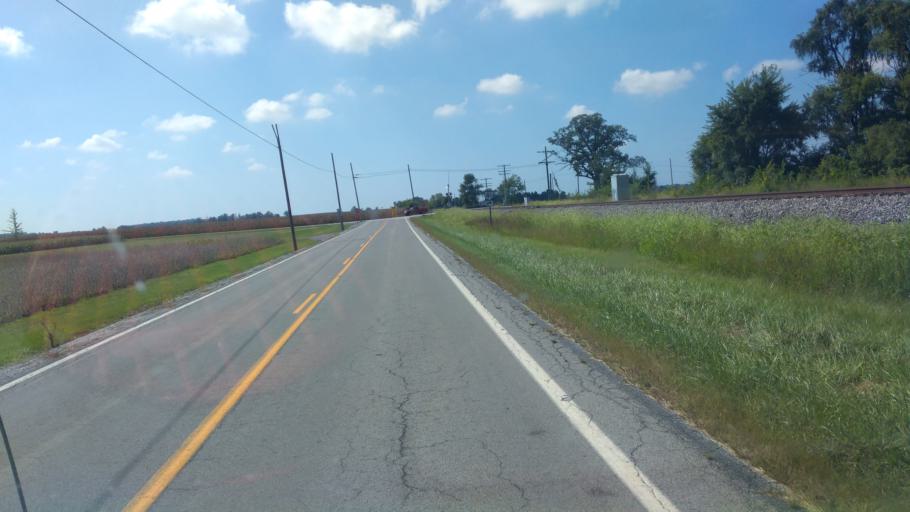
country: US
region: Ohio
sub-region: Hardin County
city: Ada
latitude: 40.7765
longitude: -83.7638
